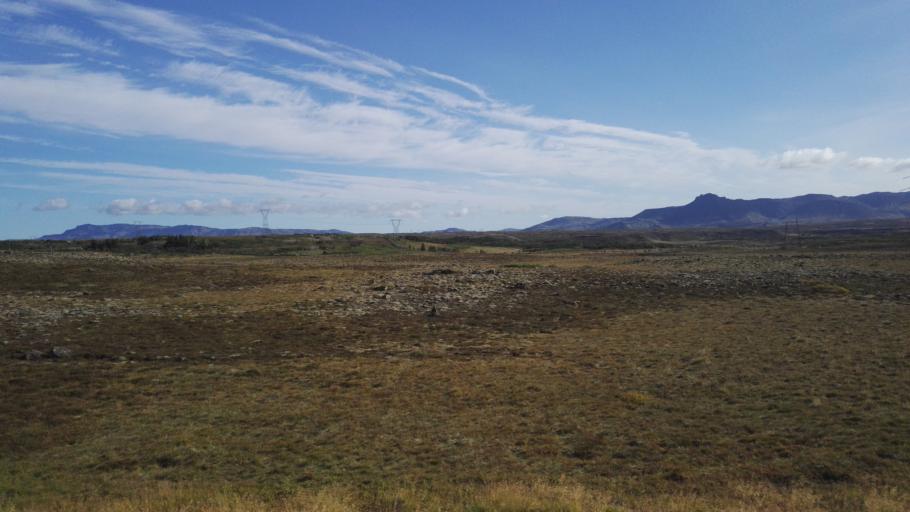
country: IS
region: Capital Region
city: Mosfellsbaer
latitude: 64.1048
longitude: -21.6823
